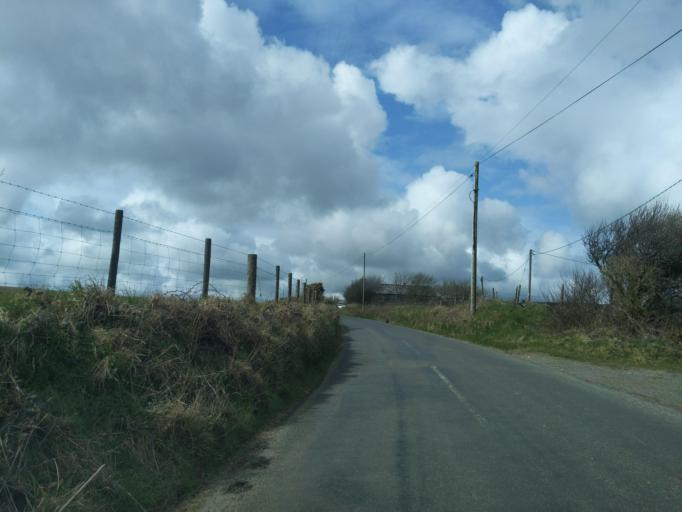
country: GB
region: England
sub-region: Cornwall
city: Camelford
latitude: 50.6265
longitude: -4.5945
